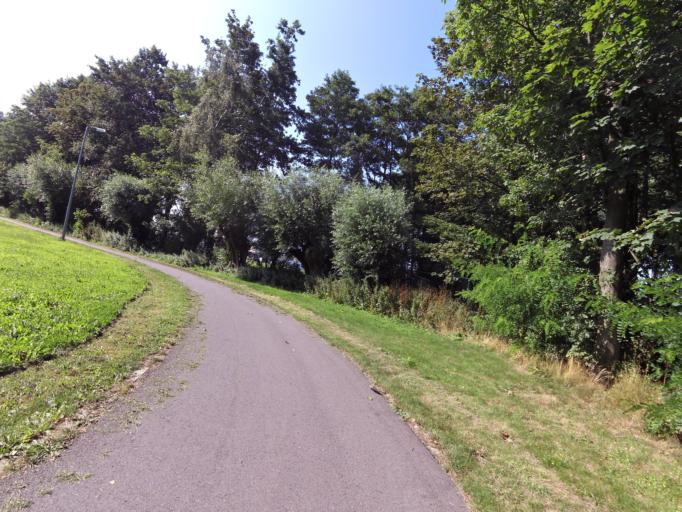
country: BE
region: Flanders
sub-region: Provincie West-Vlaanderen
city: Jabbeke
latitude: 51.1820
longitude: 3.1121
